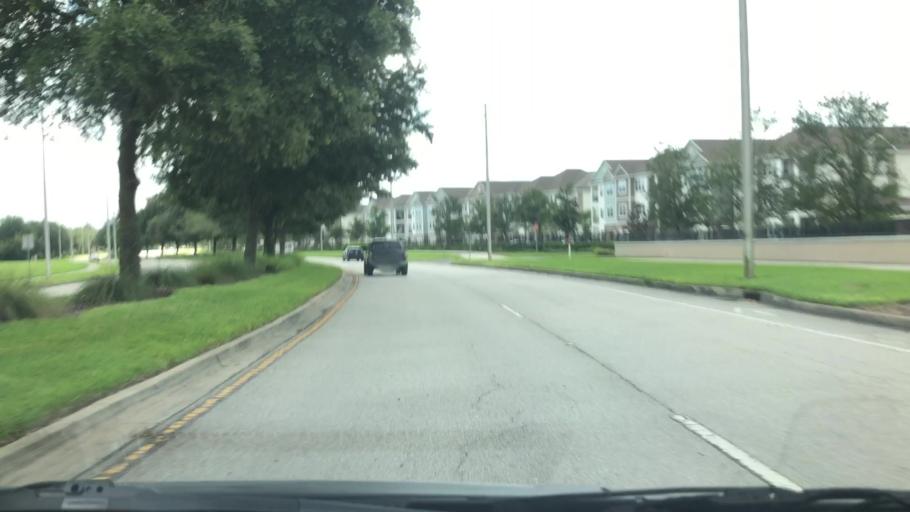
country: US
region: Florida
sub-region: Saint Johns County
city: Fruit Cove
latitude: 30.1226
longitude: -81.5295
